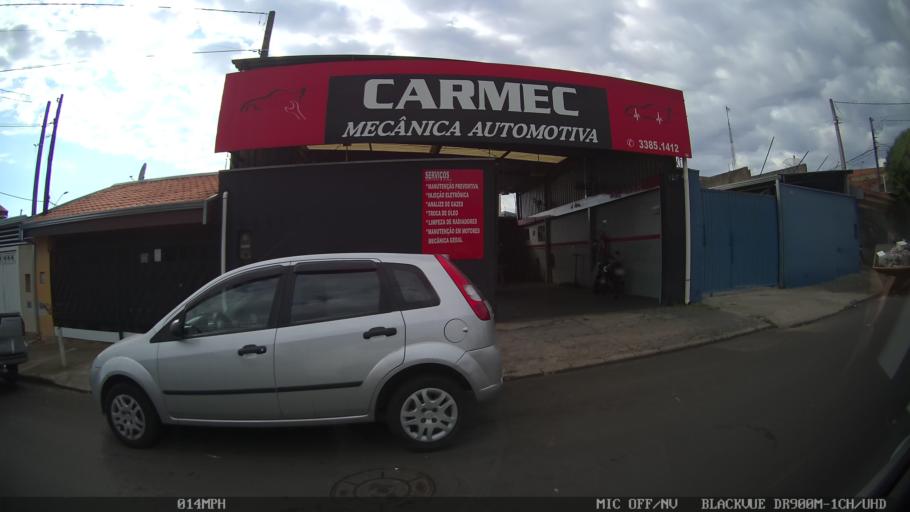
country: BR
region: Sao Paulo
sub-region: Americana
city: Americana
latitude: -22.7187
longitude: -47.3592
